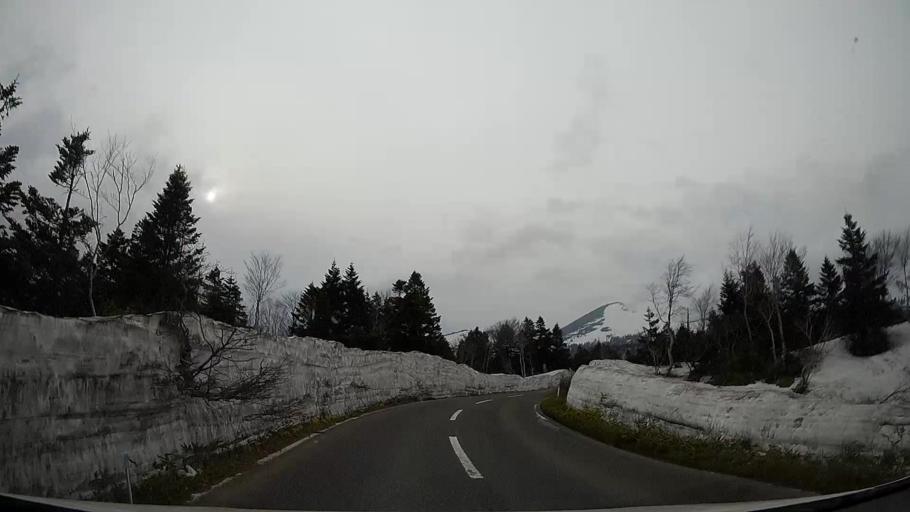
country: JP
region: Aomori
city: Aomori Shi
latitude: 40.6308
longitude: 140.8917
